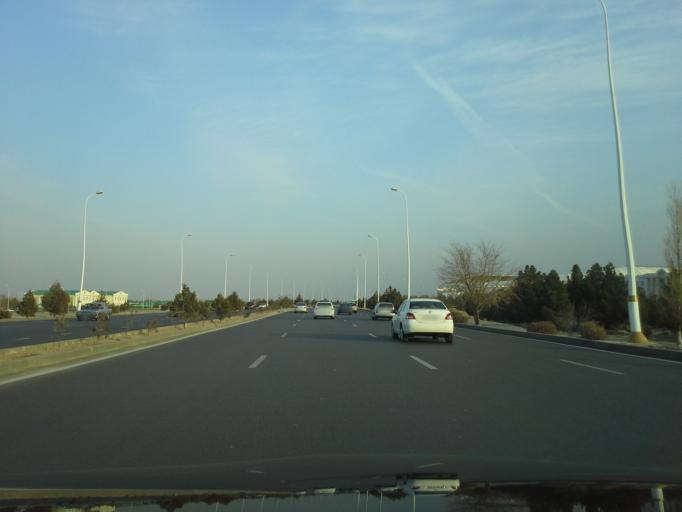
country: TM
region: Ahal
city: Abadan
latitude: 38.0489
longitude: 58.1931
